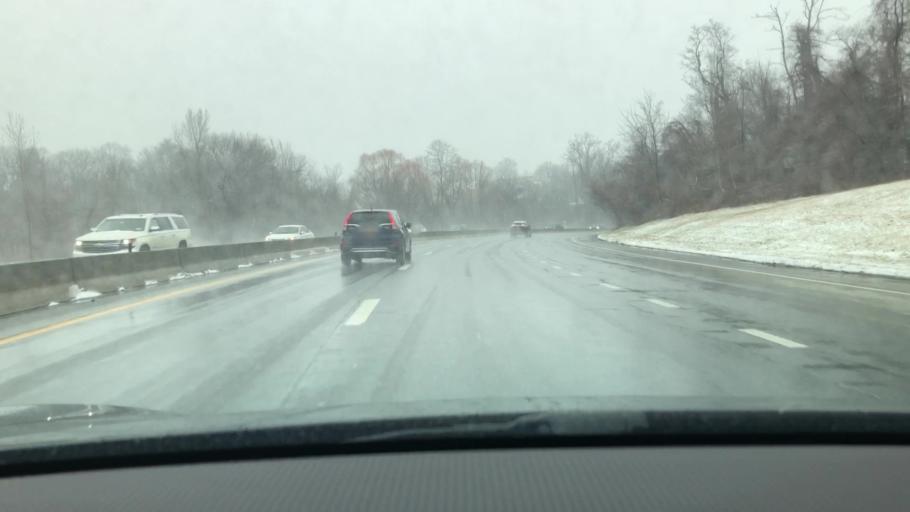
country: US
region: New York
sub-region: Westchester County
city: Tuckahoe
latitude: 40.9530
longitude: -73.7988
